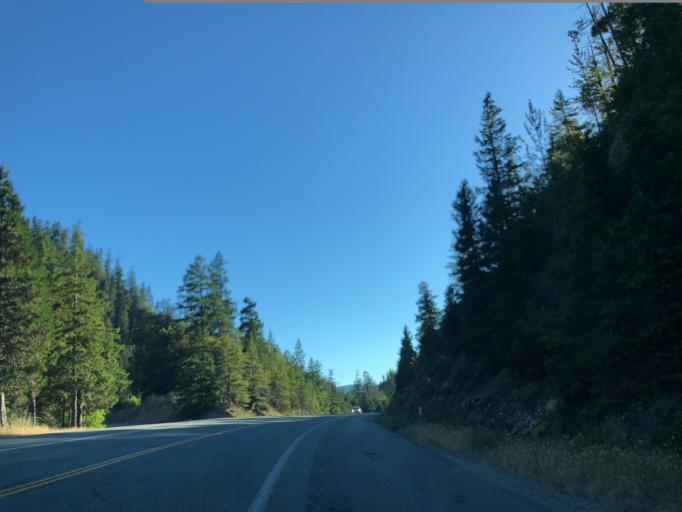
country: US
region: California
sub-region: Del Norte County
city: Bertsch-Oceanview
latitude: 41.8622
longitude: -123.8683
